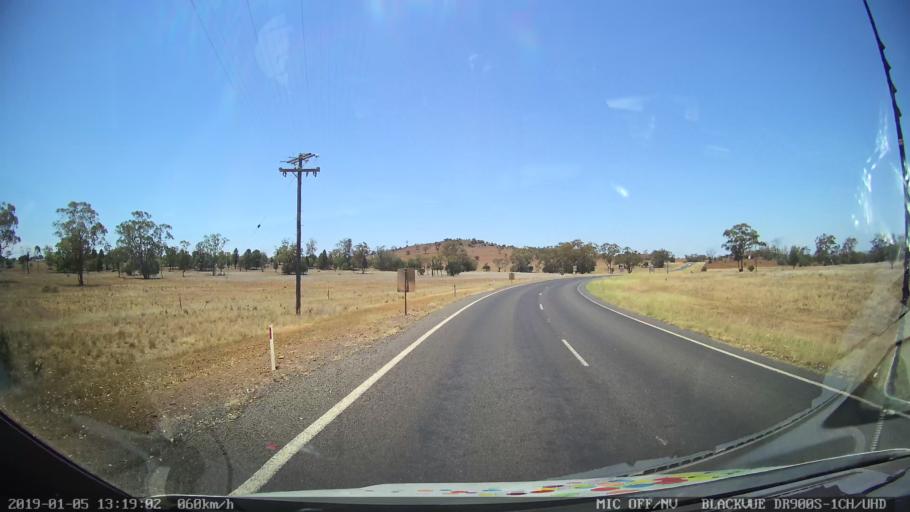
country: AU
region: New South Wales
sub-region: Gunnedah
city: Gunnedah
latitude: -31.0956
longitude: 149.9157
